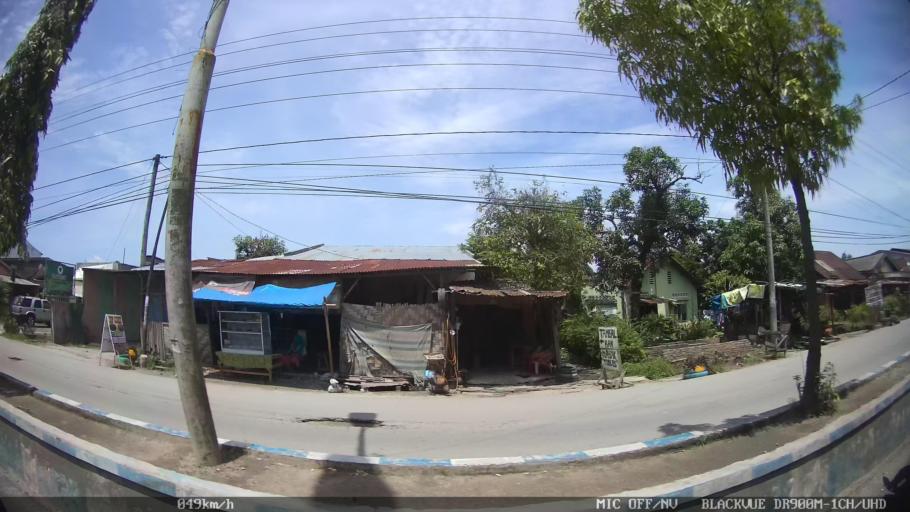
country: ID
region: North Sumatra
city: Percut
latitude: 3.5501
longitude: 98.8795
